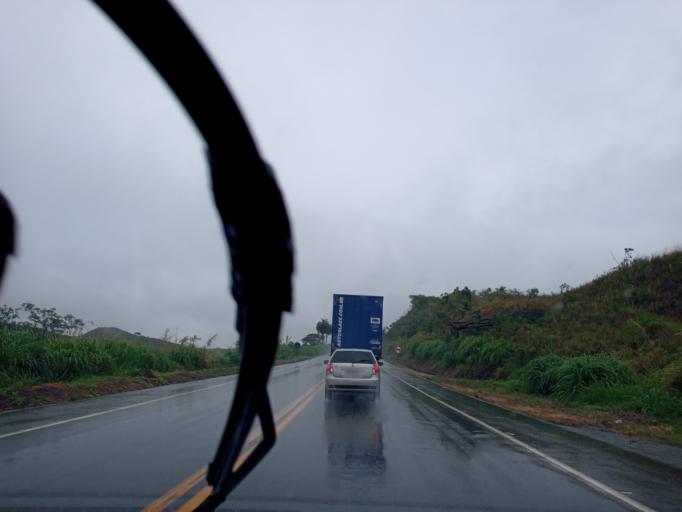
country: BR
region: Minas Gerais
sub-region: Luz
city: Luz
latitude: -19.7217
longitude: -45.8737
